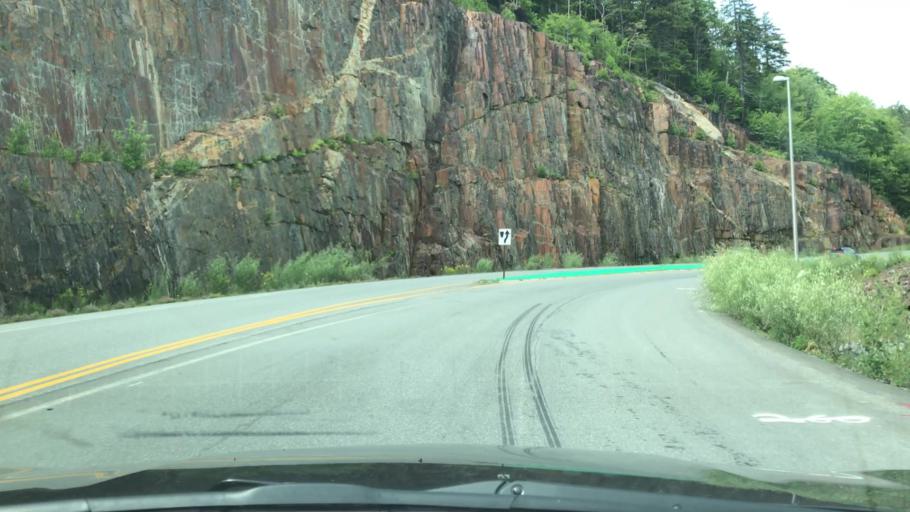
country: US
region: Maine
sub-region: Hancock County
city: Bucksport
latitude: 44.5600
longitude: -68.8072
